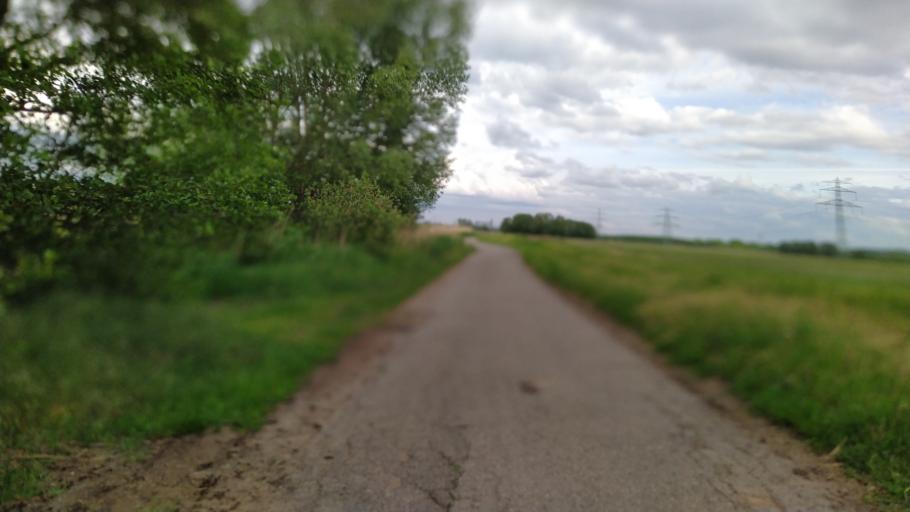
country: DE
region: Lower Saxony
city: Neu Wulmstorf
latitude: 53.4948
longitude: 9.8453
